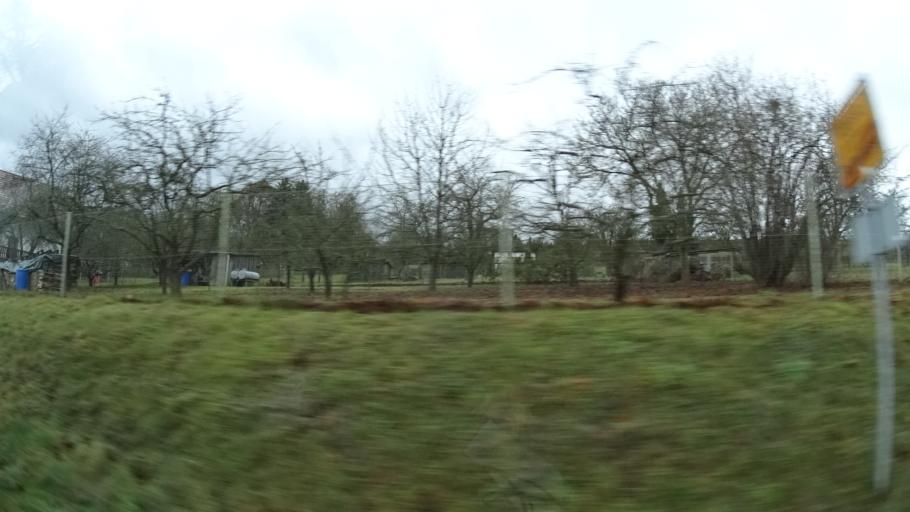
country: DE
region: Thuringia
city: Stepfershausen
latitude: 50.5975
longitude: 10.2977
